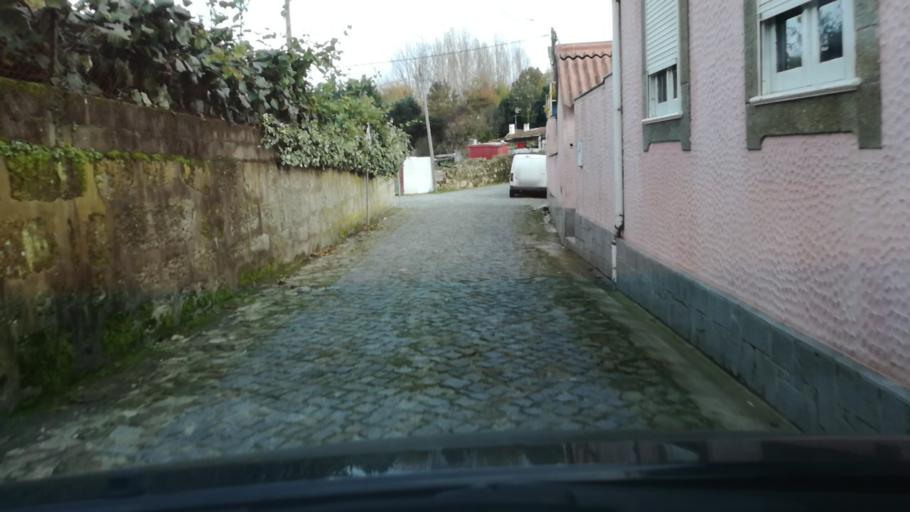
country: PT
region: Porto
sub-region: Maia
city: Gemunde
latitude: 41.2641
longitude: -8.6699
